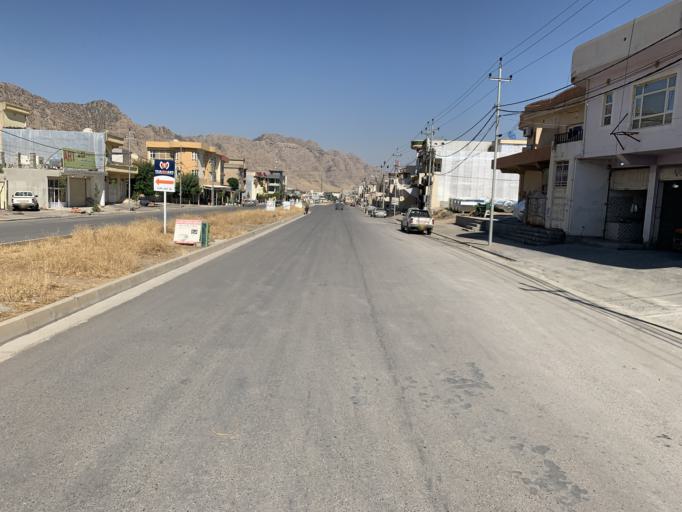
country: IQ
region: As Sulaymaniyah
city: Raniye
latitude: 36.2585
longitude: 44.8675
